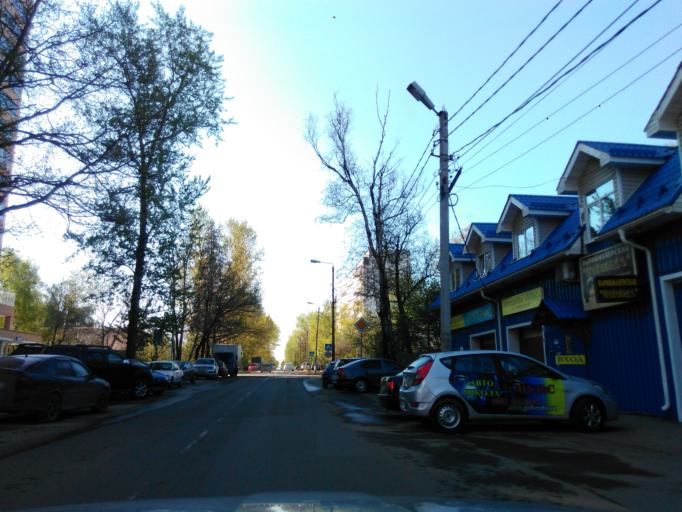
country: RU
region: Moskovskaya
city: Skhodnya
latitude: 55.9457
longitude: 37.3000
